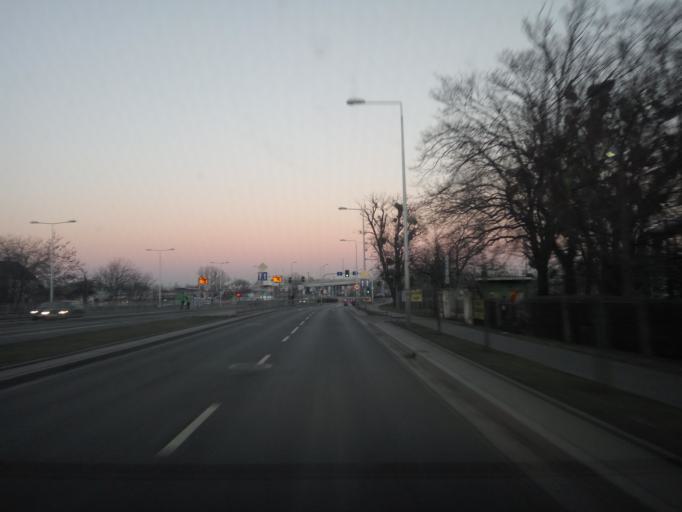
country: PL
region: Lower Silesian Voivodeship
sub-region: Powiat wroclawski
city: Wroclaw
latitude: 51.1132
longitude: 16.9639
